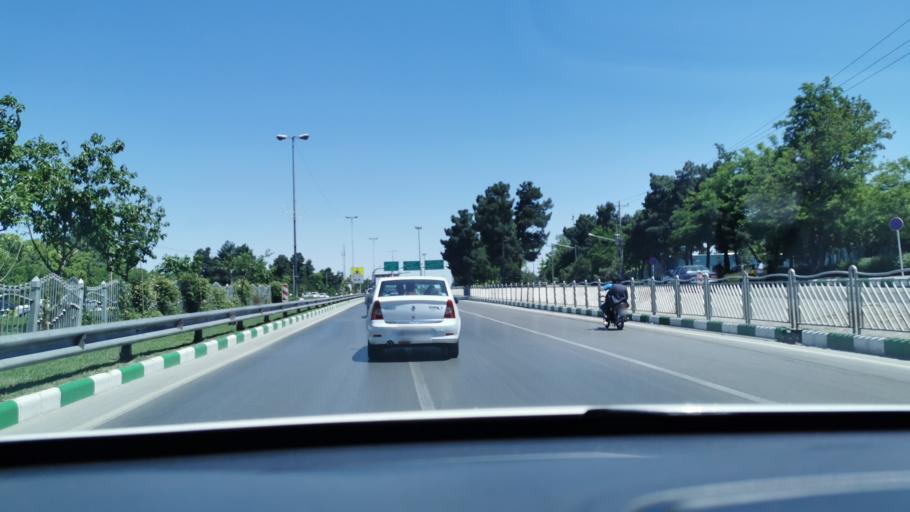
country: IR
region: Razavi Khorasan
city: Mashhad
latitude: 36.2539
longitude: 59.6031
